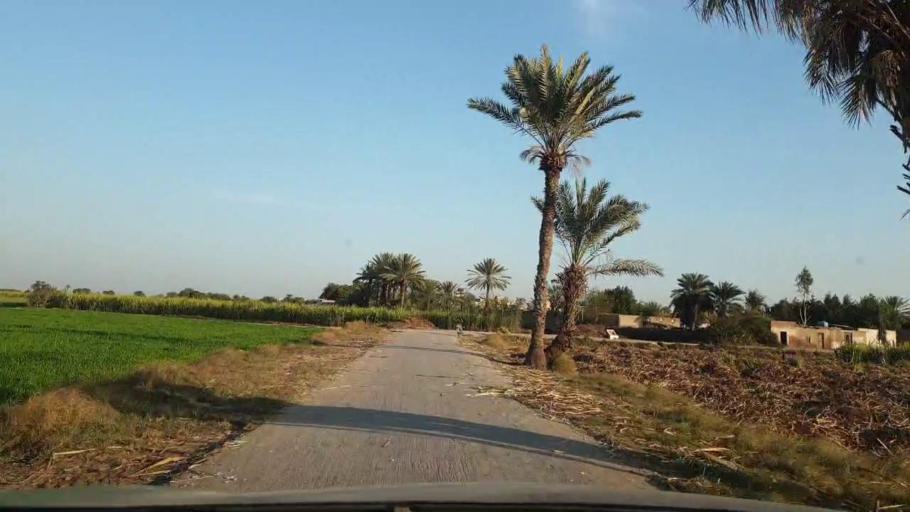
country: PK
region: Sindh
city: Tando Adam
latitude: 25.6191
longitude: 68.6712
